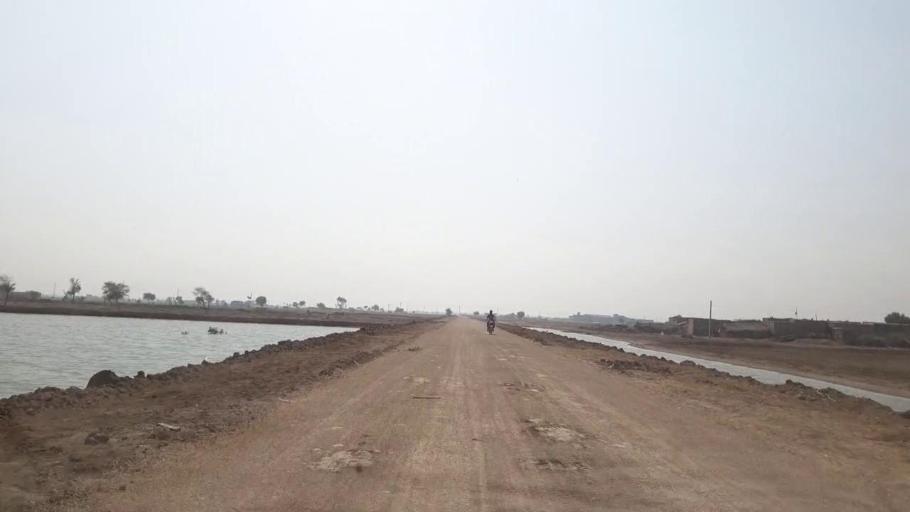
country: PK
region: Sindh
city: Mirpur Khas
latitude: 25.5579
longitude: 69.0472
